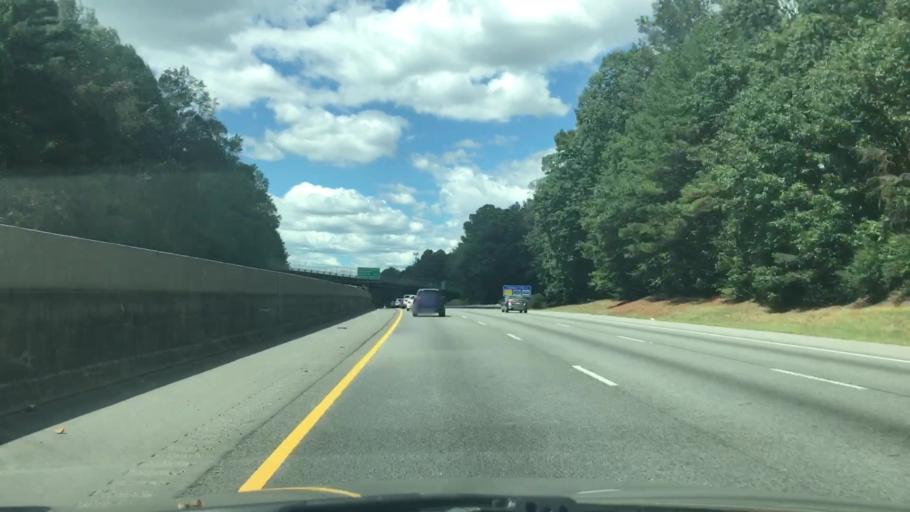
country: US
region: Georgia
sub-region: DeKalb County
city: Stone Mountain
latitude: 33.8274
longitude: -84.1763
